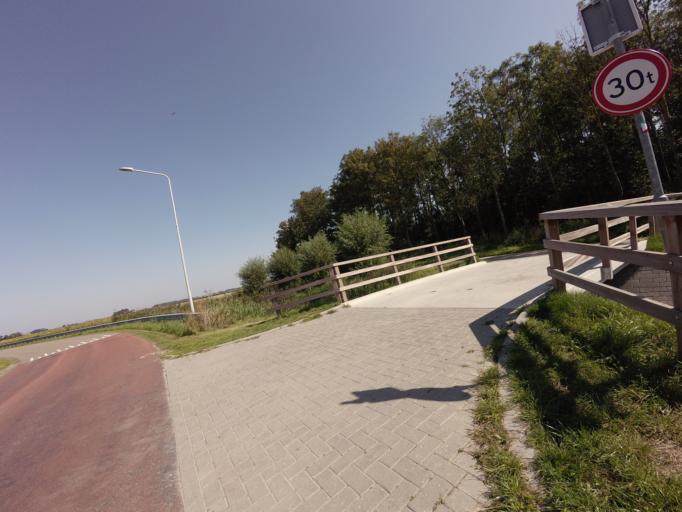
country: NL
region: Friesland
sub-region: Gemeente Dongeradeel
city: Anjum
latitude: 53.3823
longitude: 6.0558
